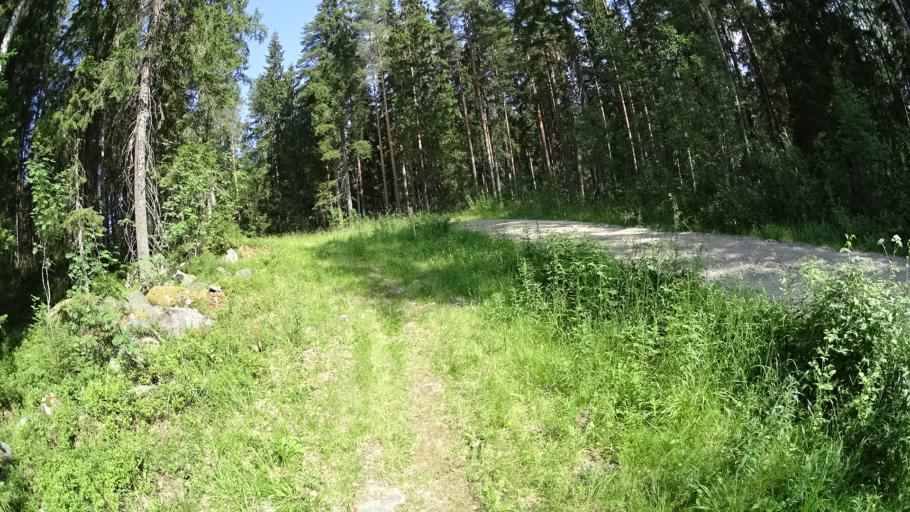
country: FI
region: North Karelia
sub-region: Pielisen Karjala
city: Lieksa
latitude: 63.1231
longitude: 29.8058
